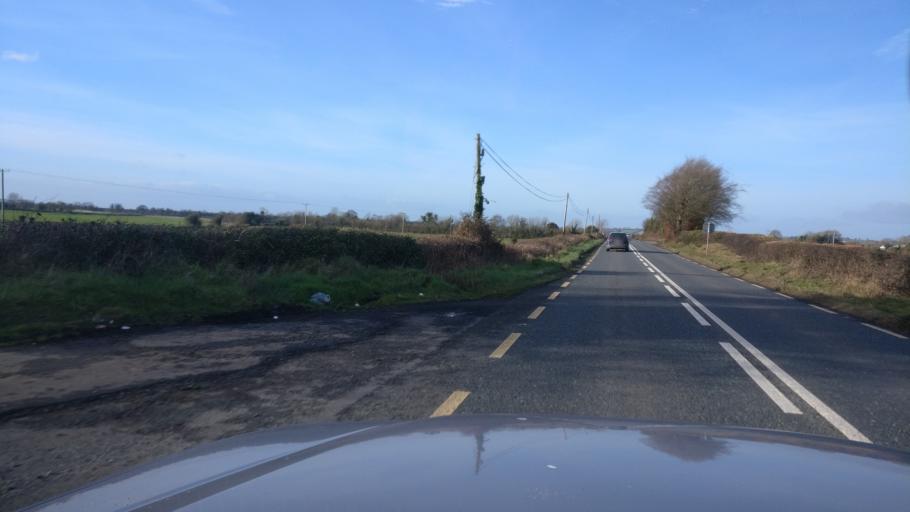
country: IE
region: Leinster
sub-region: Laois
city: Mountmellick
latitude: 53.1620
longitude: -7.3696
